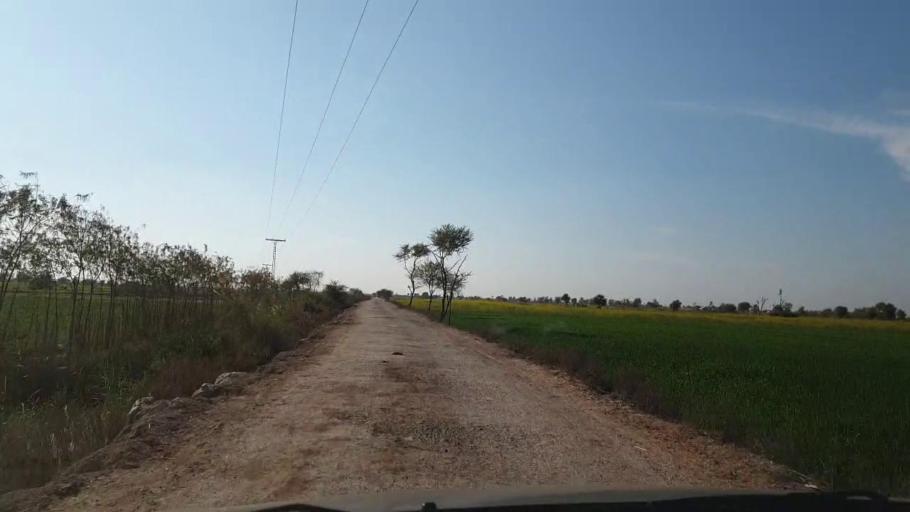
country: PK
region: Sindh
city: Khadro
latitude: 26.1552
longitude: 68.7597
